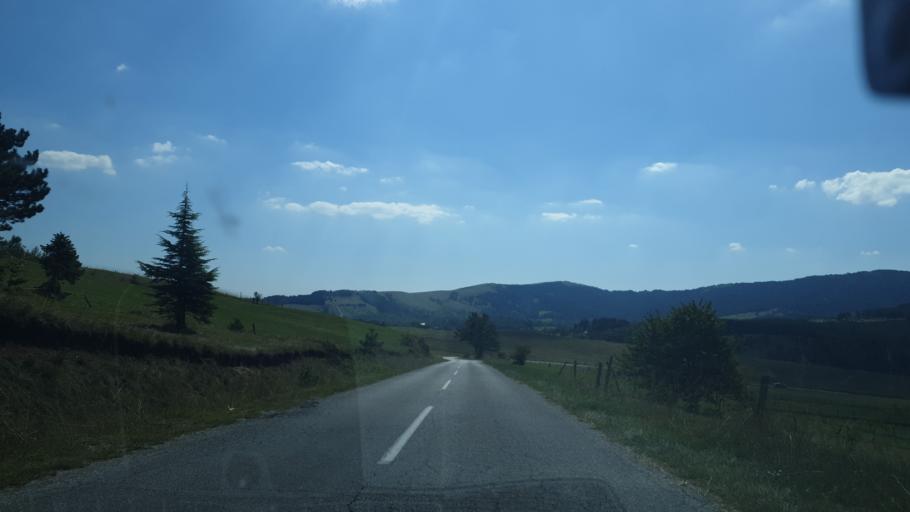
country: RS
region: Central Serbia
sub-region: Zlatiborski Okrug
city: Kosjeric
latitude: 44.0756
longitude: 20.0209
